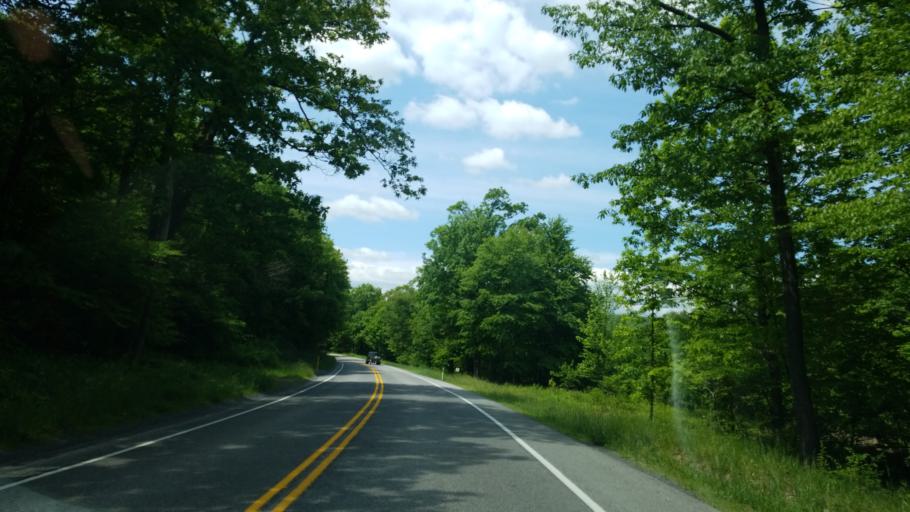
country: US
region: Pennsylvania
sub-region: Blair County
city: Tipton
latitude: 40.7102
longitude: -78.3156
